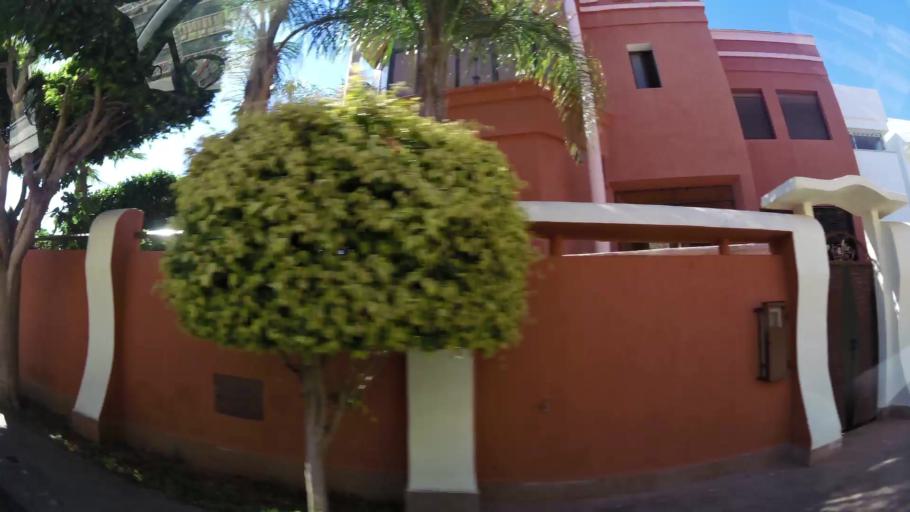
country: MA
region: Oriental
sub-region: Berkane-Taourirt
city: Berkane
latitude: 34.9451
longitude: -2.3282
